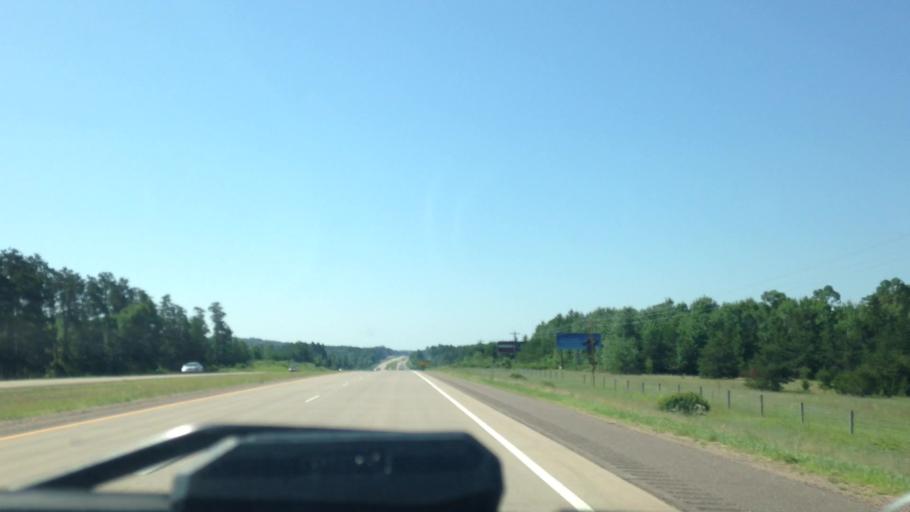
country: US
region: Wisconsin
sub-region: Washburn County
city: Spooner
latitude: 45.9204
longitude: -91.8280
